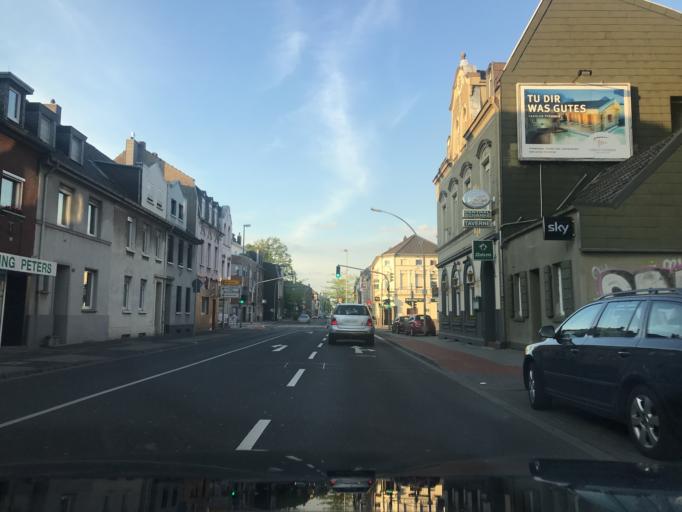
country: DE
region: North Rhine-Westphalia
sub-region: Regierungsbezirk Dusseldorf
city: Monchengladbach
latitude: 51.1808
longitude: 6.4078
